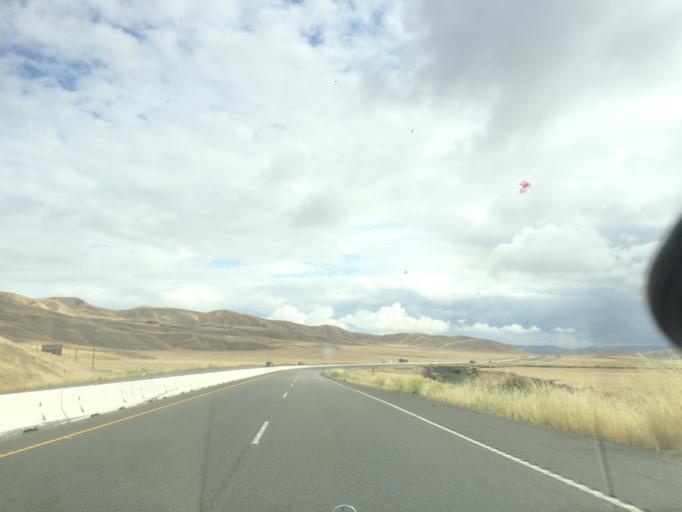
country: US
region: California
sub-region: San Luis Obispo County
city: Shandon
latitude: 35.7009
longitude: -120.3236
